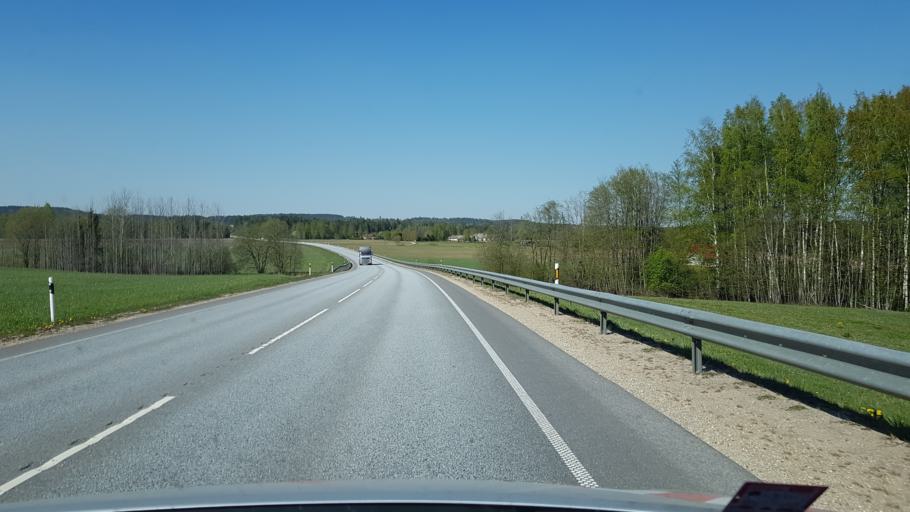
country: EE
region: Tartu
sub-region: UElenurme vald
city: Ulenurme
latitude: 58.2039
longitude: 26.7077
